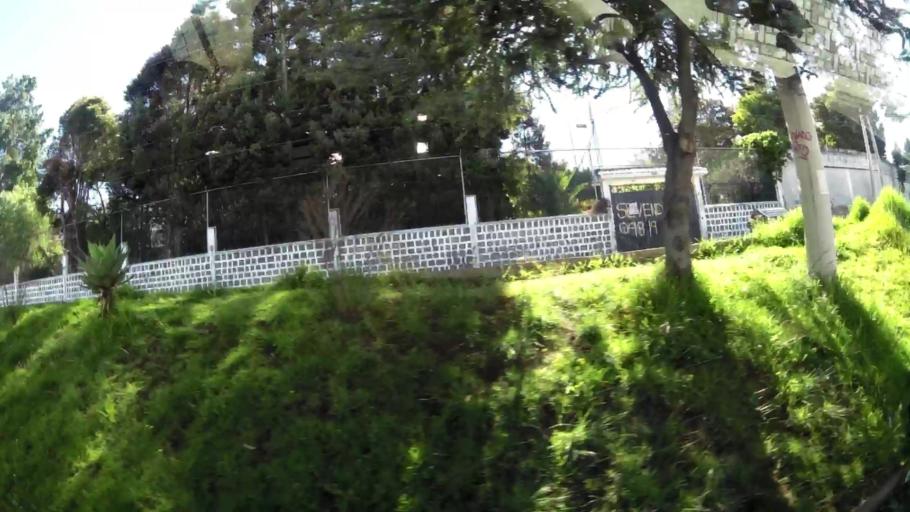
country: EC
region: Pichincha
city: Quito
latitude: -0.1249
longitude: -78.4761
